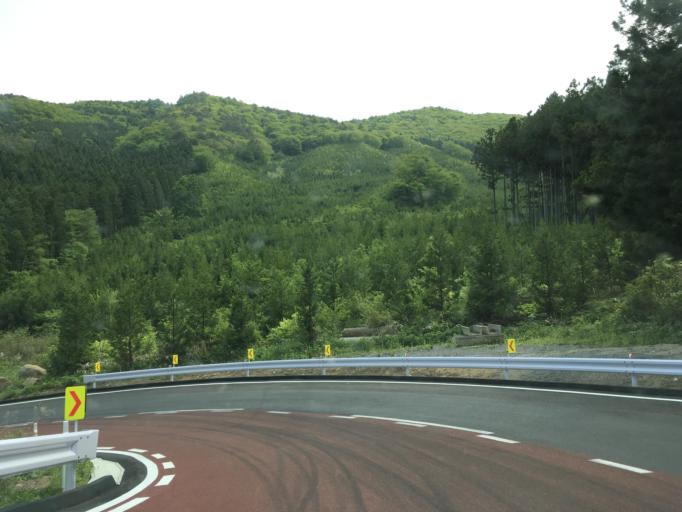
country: JP
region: Iwate
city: Ofunato
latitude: 38.8549
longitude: 141.4814
